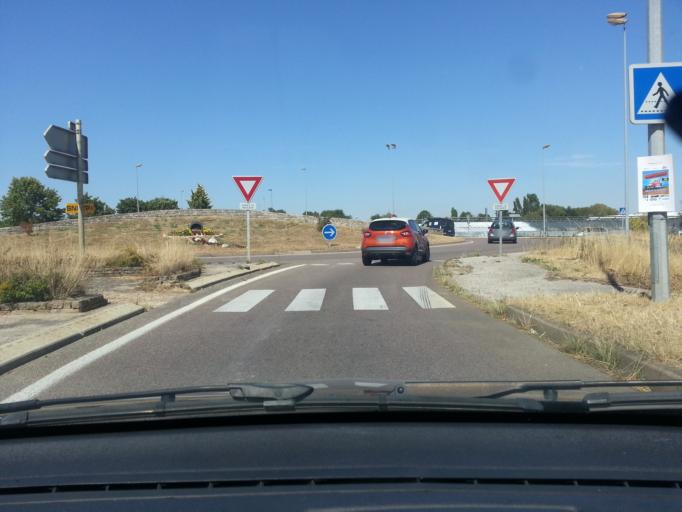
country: FR
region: Bourgogne
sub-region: Departement de la Cote-d'Or
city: Couchey
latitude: 47.2434
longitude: 4.9877
